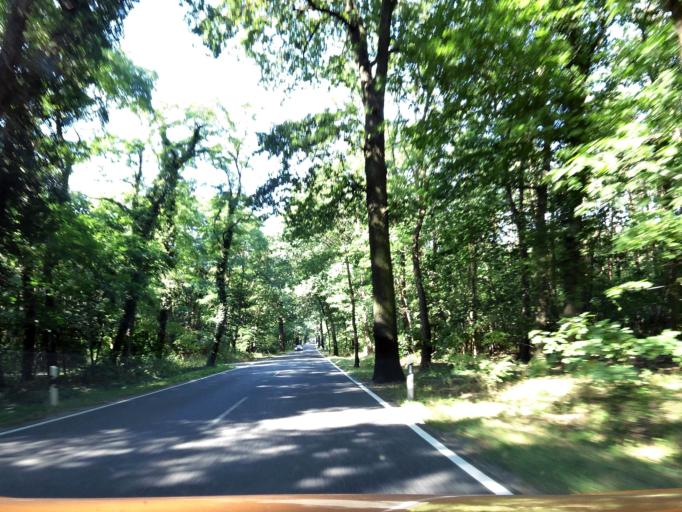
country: DE
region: Brandenburg
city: Teltow
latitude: 52.3673
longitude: 13.2654
